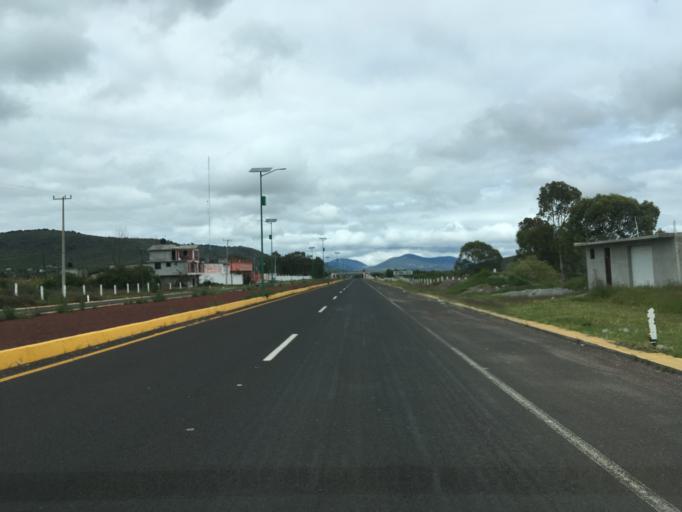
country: MX
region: Hidalgo
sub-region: Atotonilco el Grande
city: La Estancia
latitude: 20.3121
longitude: -98.6879
